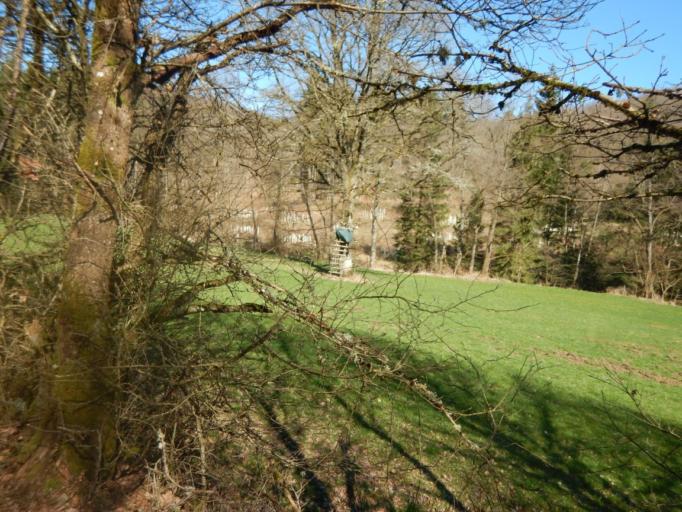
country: LU
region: Diekirch
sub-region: Canton de Wiltz
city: Eschweiler
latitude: 49.9826
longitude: 5.9689
